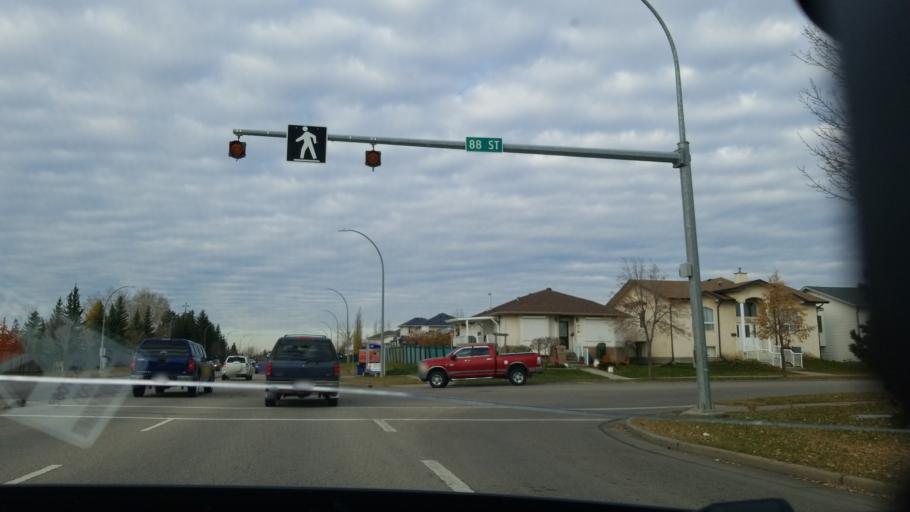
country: CA
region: Alberta
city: Edmonton
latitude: 53.6158
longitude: -113.4759
